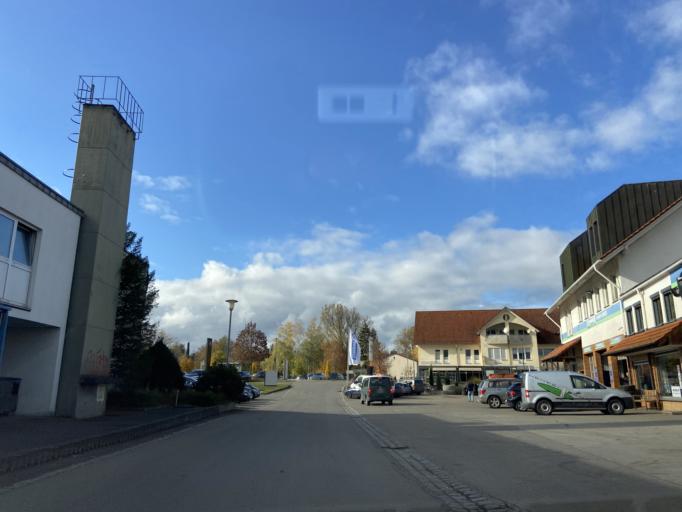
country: DE
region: Baden-Wuerttemberg
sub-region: Tuebingen Region
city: Inzigkofen
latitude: 48.0767
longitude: 9.1961
